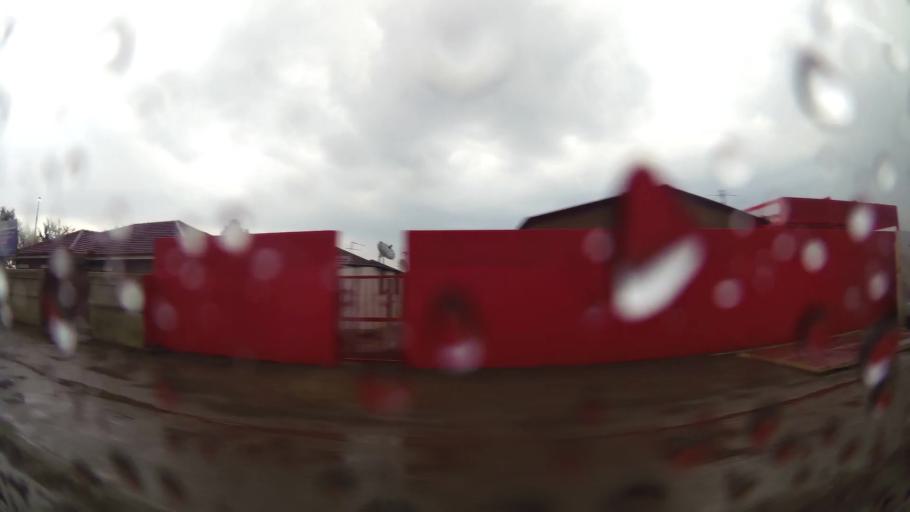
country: ZA
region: Gauteng
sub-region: Ekurhuleni Metropolitan Municipality
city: Germiston
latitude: -26.3485
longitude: 28.1345
